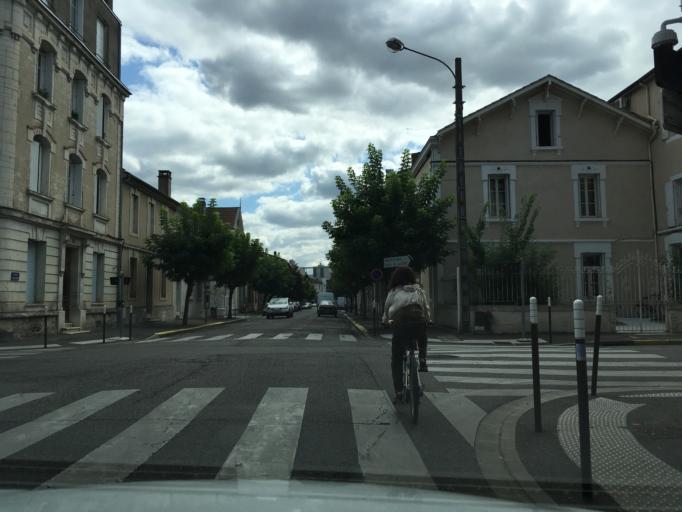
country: FR
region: Aquitaine
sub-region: Departement du Lot-et-Garonne
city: Agen
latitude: 44.1995
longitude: 0.6204
